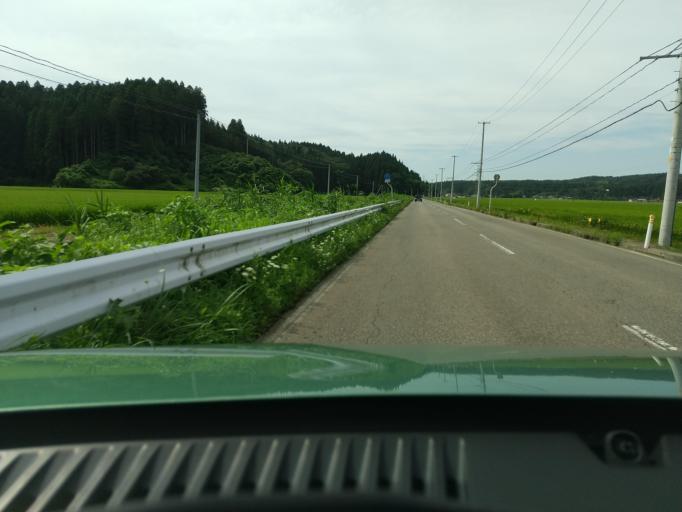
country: JP
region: Akita
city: Akita
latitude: 39.7850
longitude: 140.1244
